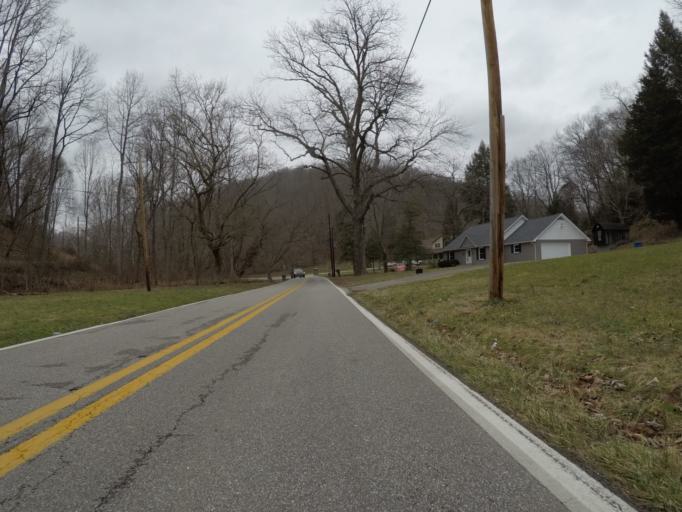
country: US
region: West Virginia
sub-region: Cabell County
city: Barboursville
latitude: 38.4447
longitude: -82.2463
